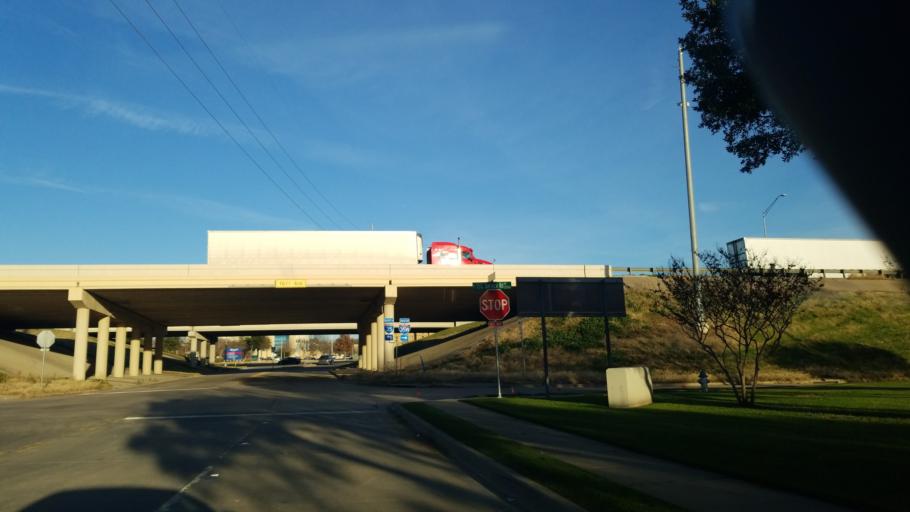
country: US
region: Texas
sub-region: Denton County
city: Denton
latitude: 33.2151
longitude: -97.1697
